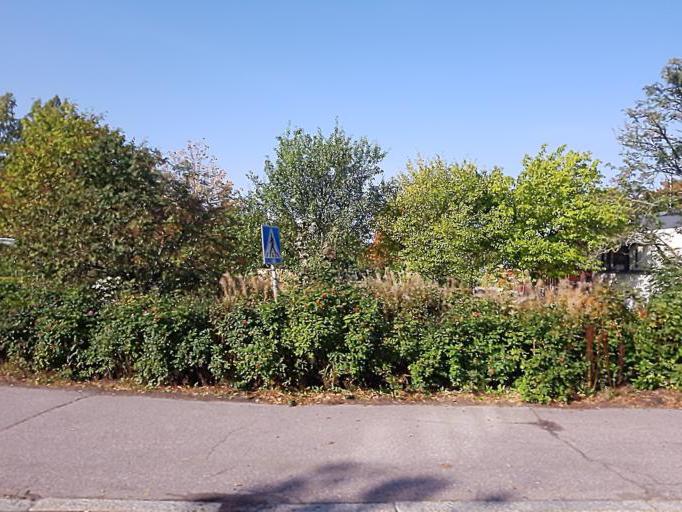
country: FI
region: Uusimaa
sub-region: Helsinki
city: Teekkarikylae
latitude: 60.2423
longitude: 24.8770
